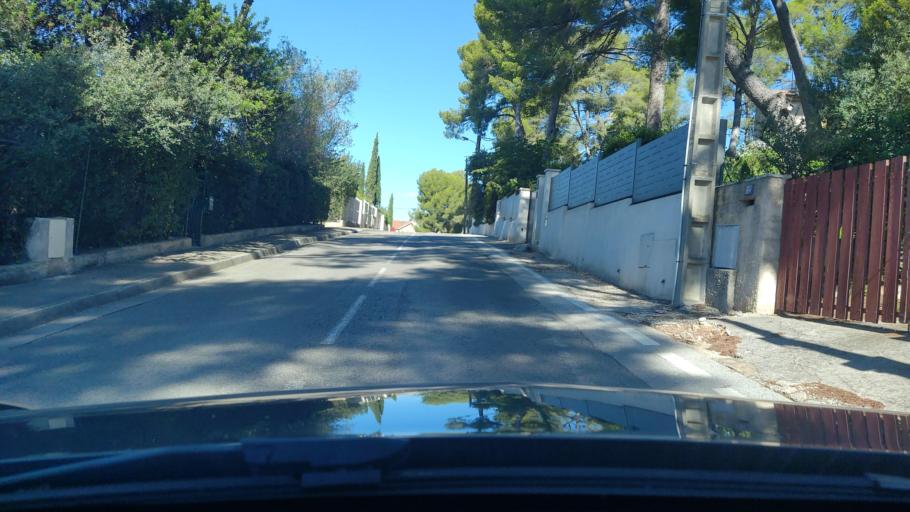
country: FR
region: Provence-Alpes-Cote d'Azur
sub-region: Departement du Var
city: Sanary-sur-Mer
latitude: 43.1182
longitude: 5.7873
